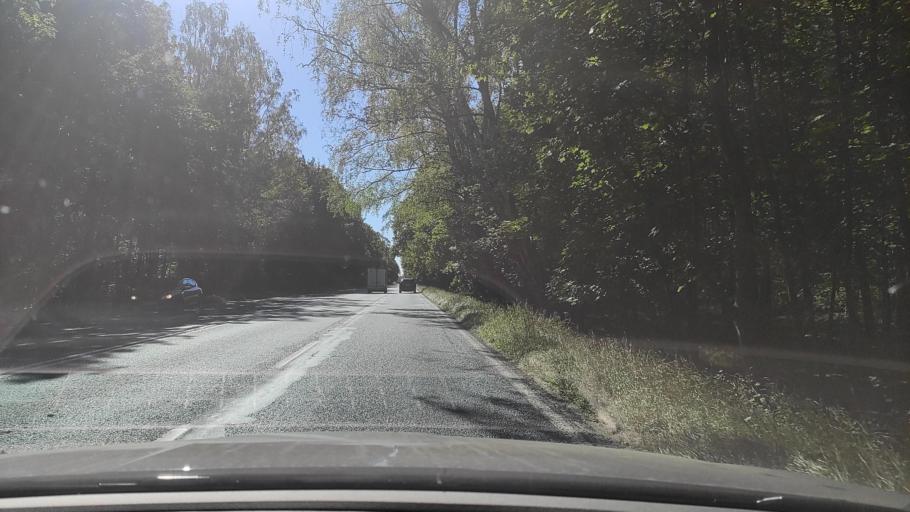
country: PL
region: Greater Poland Voivodeship
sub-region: Powiat poznanski
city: Czerwonak
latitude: 52.4231
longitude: 17.0160
